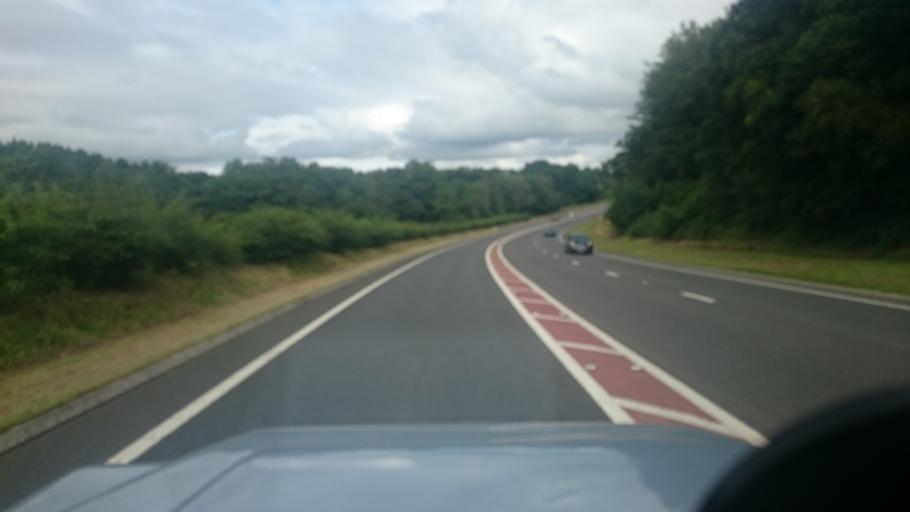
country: GB
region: Wales
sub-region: Pembrokeshire
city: Wiston
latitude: 51.8023
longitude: -4.8142
